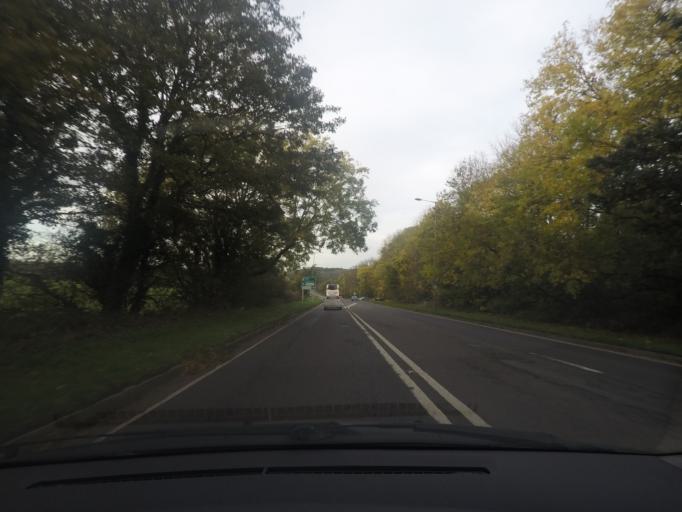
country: GB
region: England
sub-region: Sheffield
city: Chapletown
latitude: 53.4756
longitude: -1.5009
